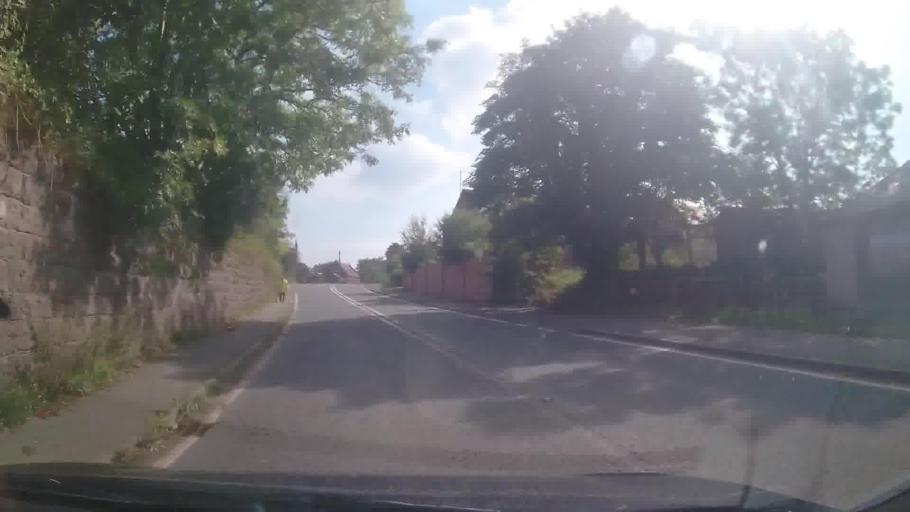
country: GB
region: England
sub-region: Cheshire West and Chester
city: Tiverton
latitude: 53.1338
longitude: -2.6702
